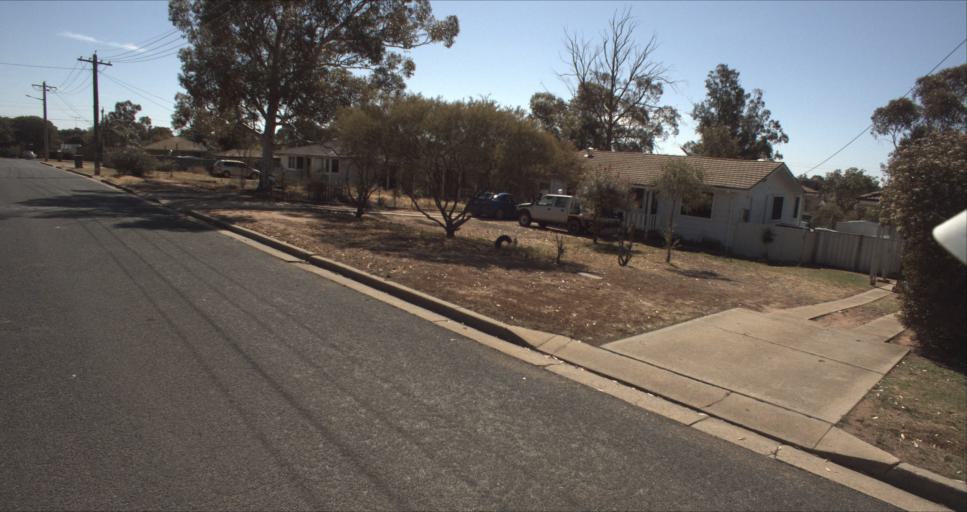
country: AU
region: New South Wales
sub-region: Leeton
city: Leeton
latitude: -34.5490
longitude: 146.3759
